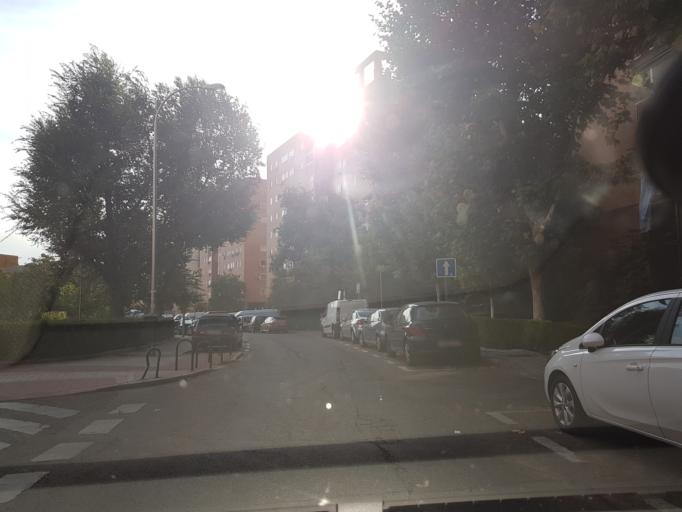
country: ES
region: Madrid
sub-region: Provincia de Madrid
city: Puente de Vallecas
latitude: 40.4051
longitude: -3.6618
